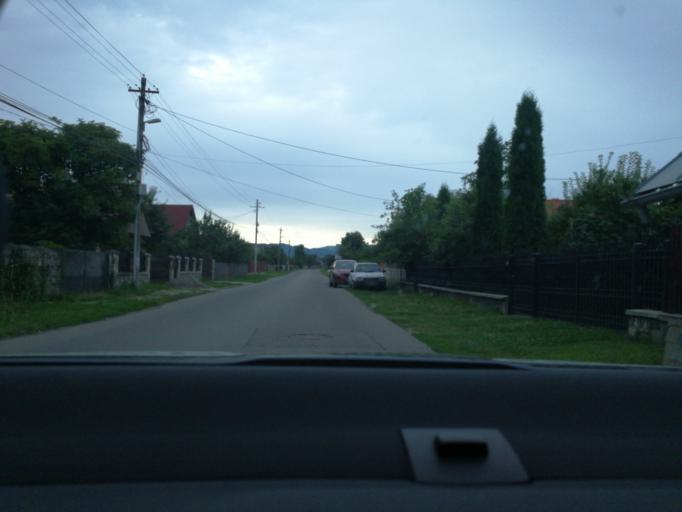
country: RO
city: Brebu Manastirei
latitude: 45.1773
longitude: 25.7648
